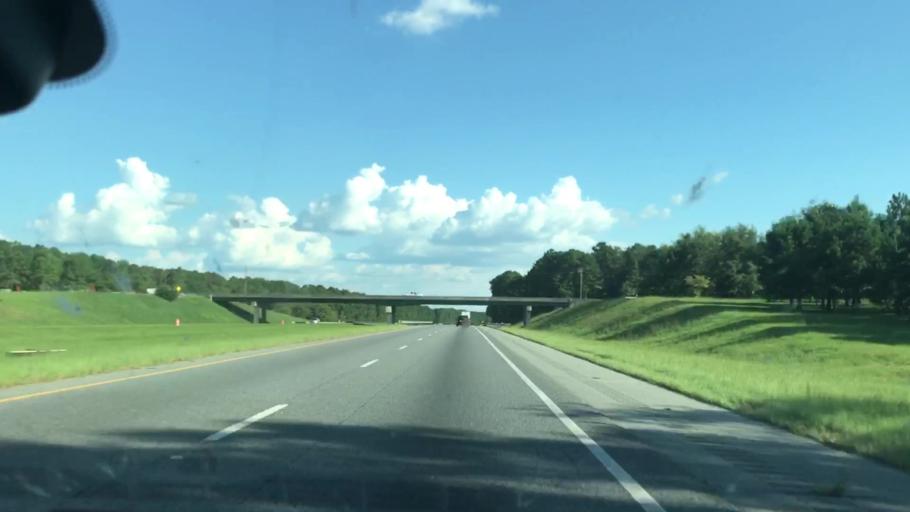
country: US
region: Georgia
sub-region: Harris County
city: Hamilton
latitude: 32.6641
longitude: -84.9822
